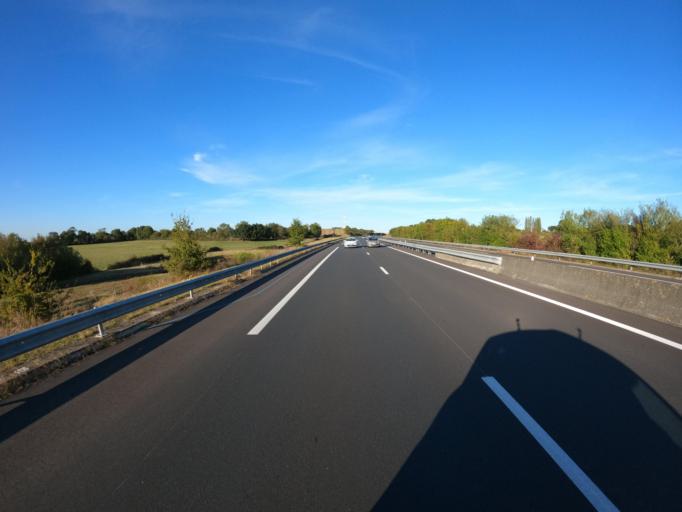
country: FR
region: Pays de la Loire
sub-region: Departement de la Vendee
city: Mortagne-sur-Sevre
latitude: 47.0010
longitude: -0.9074
